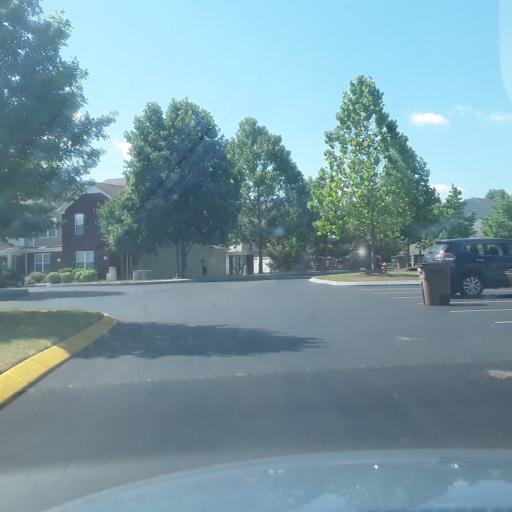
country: US
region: Tennessee
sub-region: Williamson County
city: Brentwood Estates
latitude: 36.0322
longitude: -86.7055
